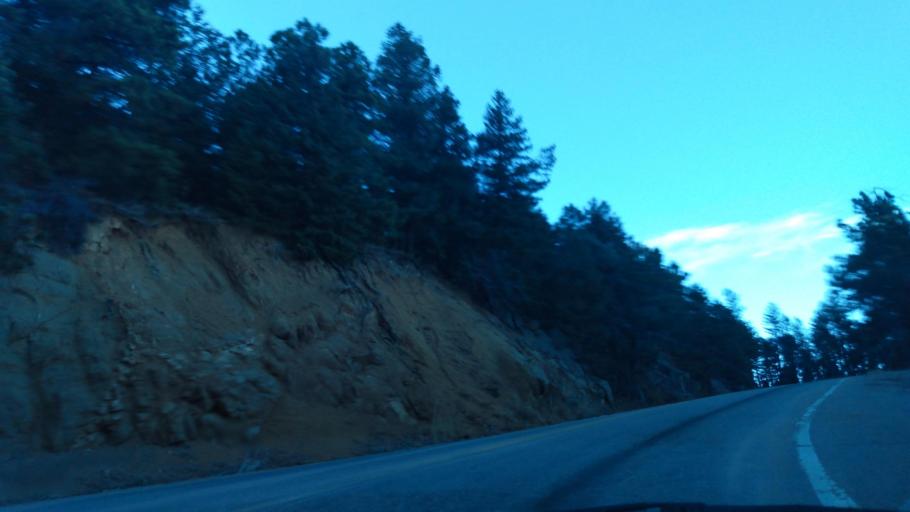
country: US
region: Colorado
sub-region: Boulder County
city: Coal Creek
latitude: 39.9840
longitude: -105.3746
